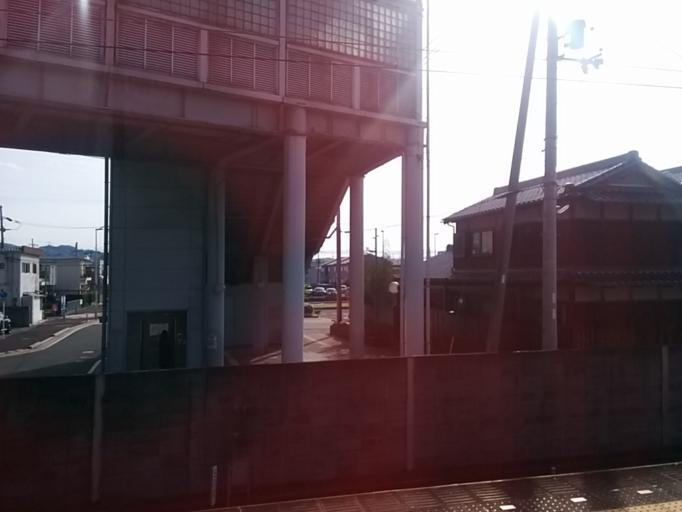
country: JP
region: Kyoto
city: Tanabe
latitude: 34.7600
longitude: 135.7927
